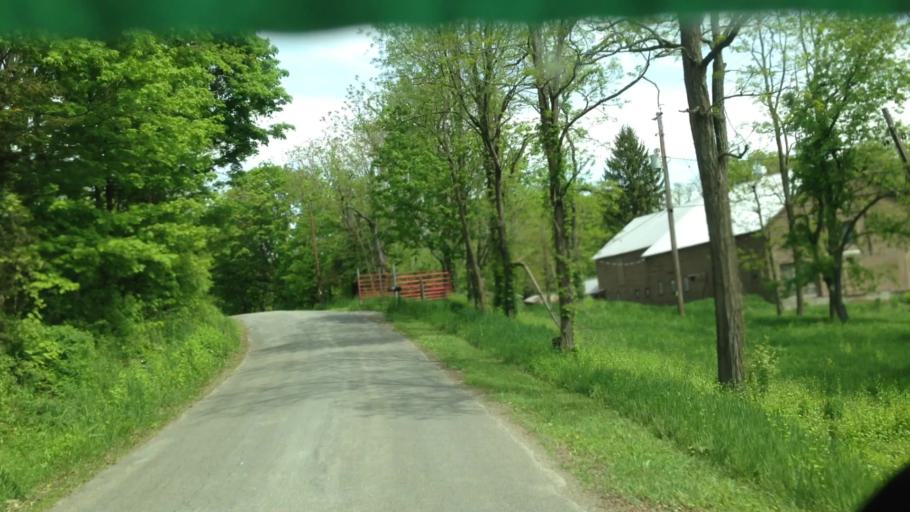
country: US
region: New York
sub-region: Dutchess County
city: Pine Plains
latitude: 41.9248
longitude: -73.7617
